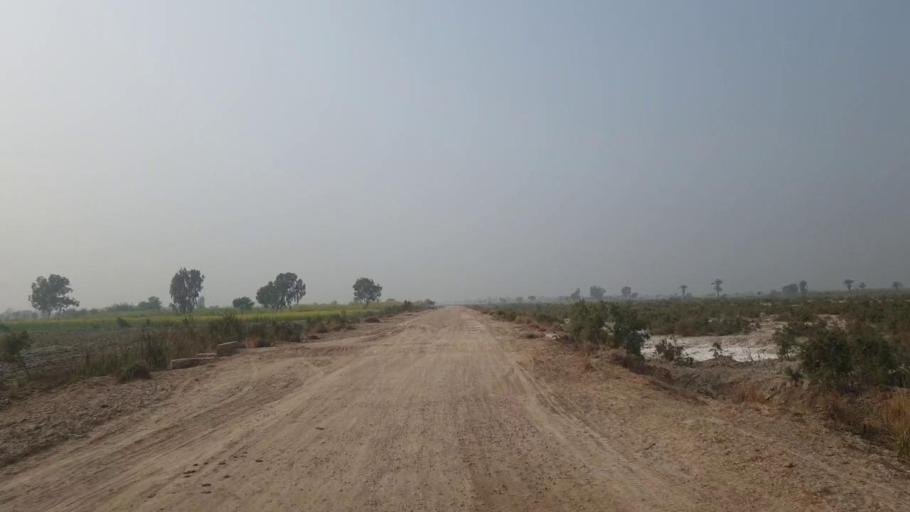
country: PK
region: Sindh
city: Shahdadpur
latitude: 25.8363
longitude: 68.5878
